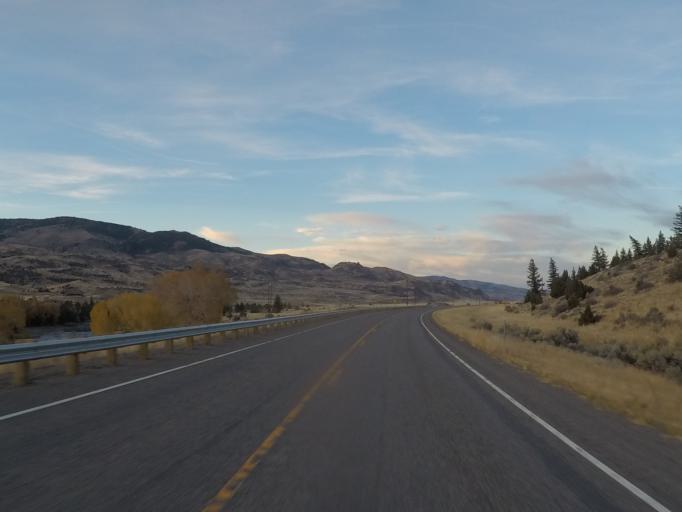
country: US
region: Montana
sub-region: Gallatin County
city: Big Sky
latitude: 45.1982
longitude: -110.9001
